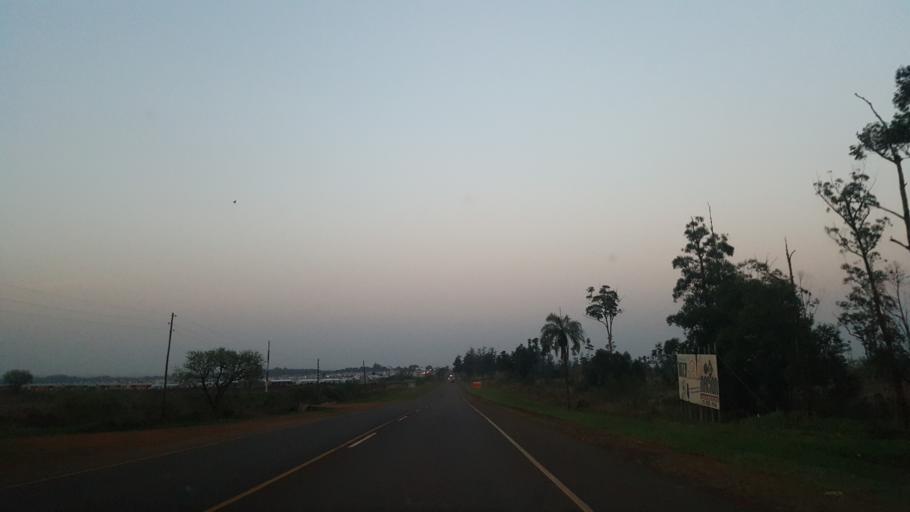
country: AR
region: Misiones
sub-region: Departamento de Capital
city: Posadas
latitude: -27.4203
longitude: -55.9923
